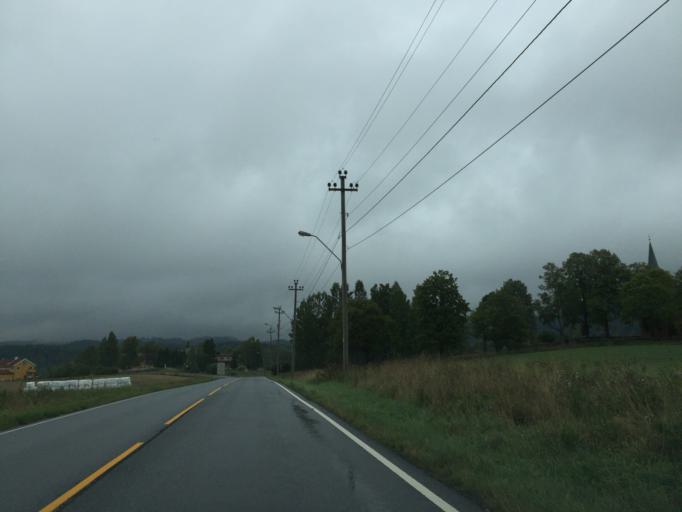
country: NO
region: Akershus
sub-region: Baerum
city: Lysaker
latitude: 60.0143
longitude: 10.6155
